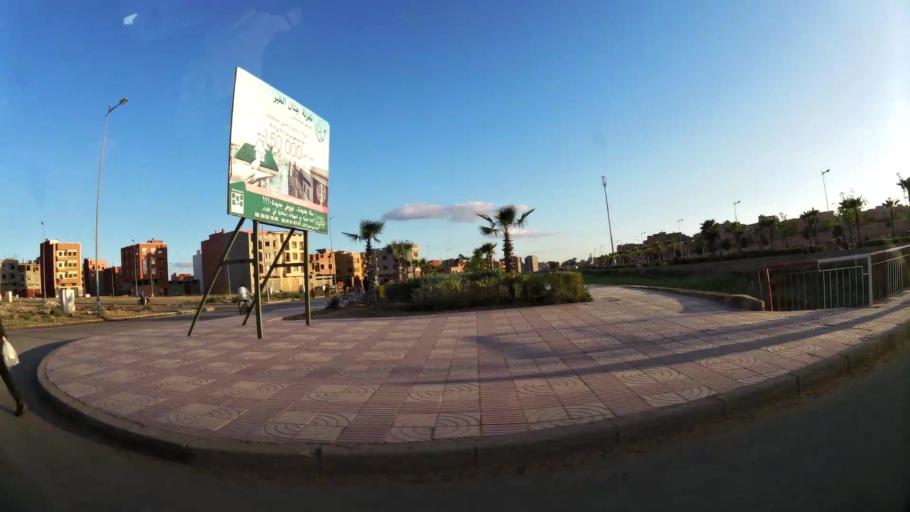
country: MA
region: Marrakech-Tensift-Al Haouz
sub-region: Kelaa-Des-Sraghna
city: Sidi Abdallah
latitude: 32.2394
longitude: -7.9488
